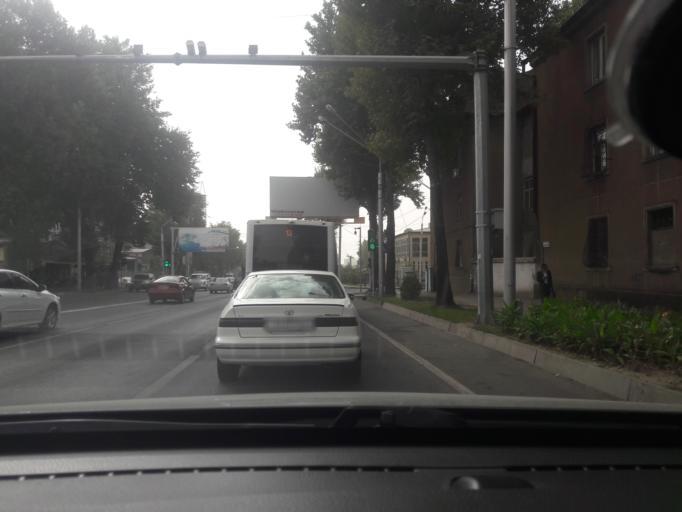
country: TJ
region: Dushanbe
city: Dushanbe
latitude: 38.5758
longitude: 68.8043
